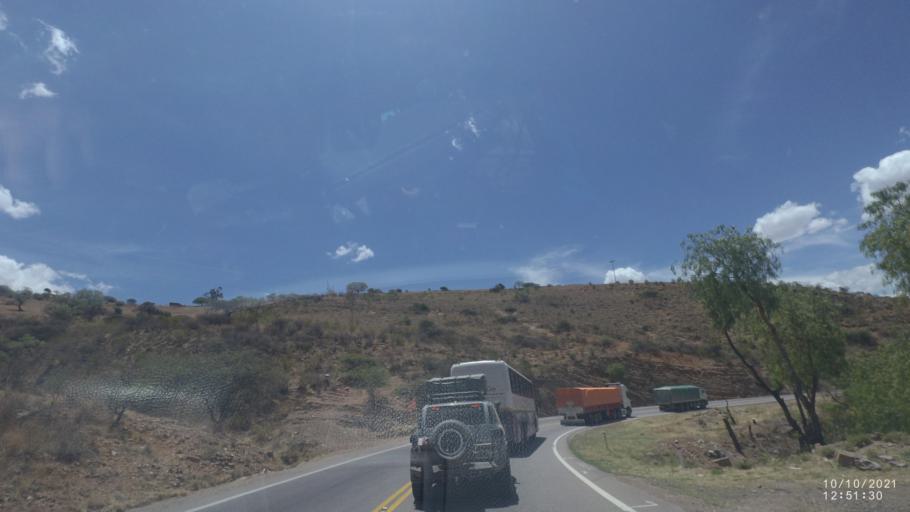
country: BO
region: Cochabamba
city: Irpa Irpa
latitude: -17.6175
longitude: -66.3619
